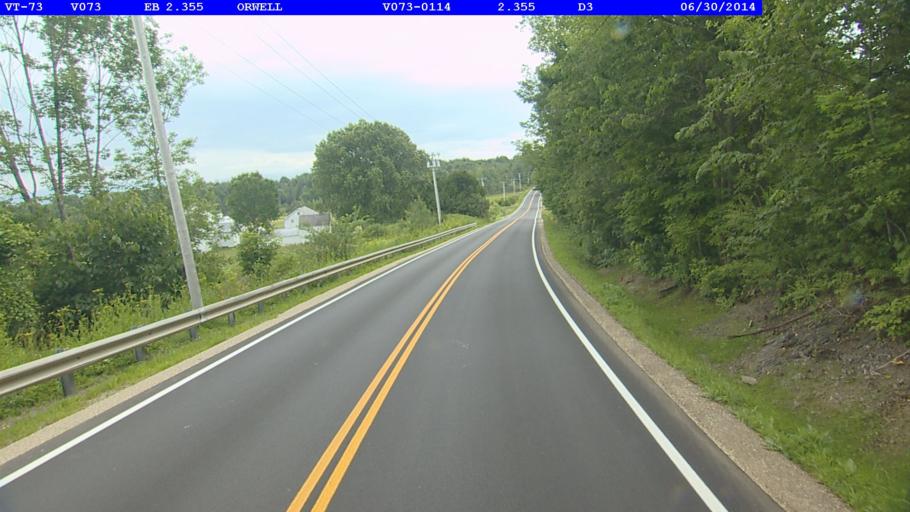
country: US
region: New York
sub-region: Essex County
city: Ticonderoga
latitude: 43.8037
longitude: -73.2594
